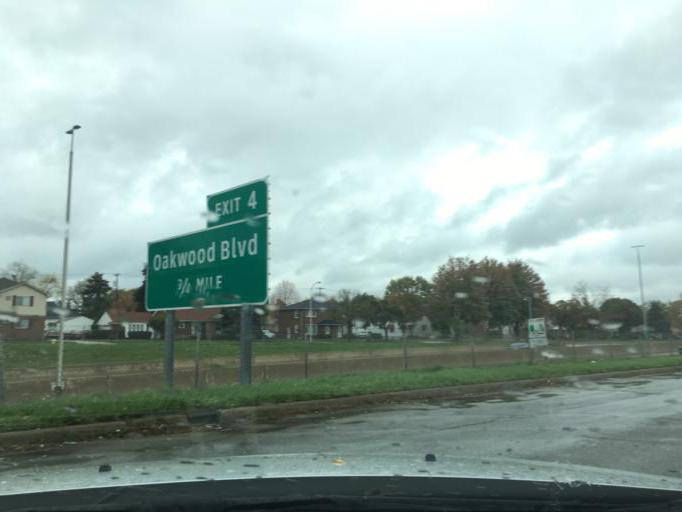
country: US
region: Michigan
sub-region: Wayne County
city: Allen Park
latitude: 42.2786
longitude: -83.2160
